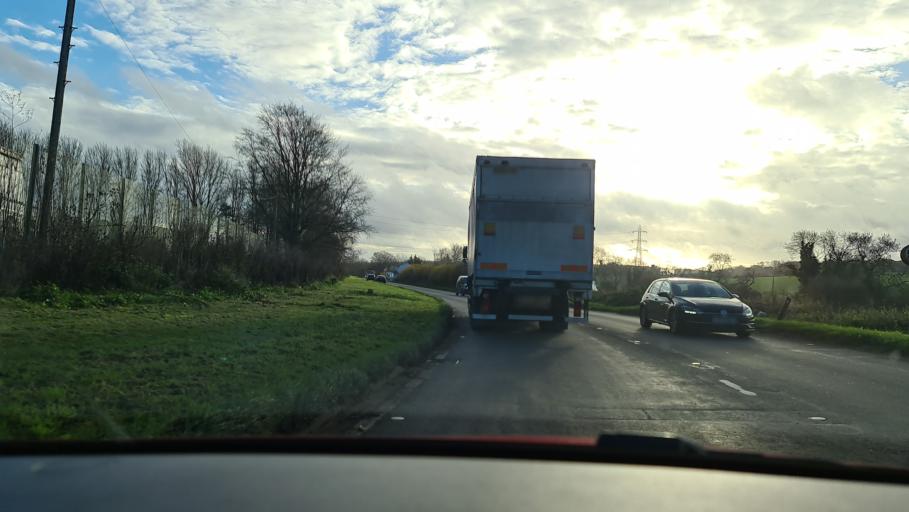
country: GB
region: England
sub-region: Buckinghamshire
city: Great Missenden
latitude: 51.6869
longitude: -0.6868
